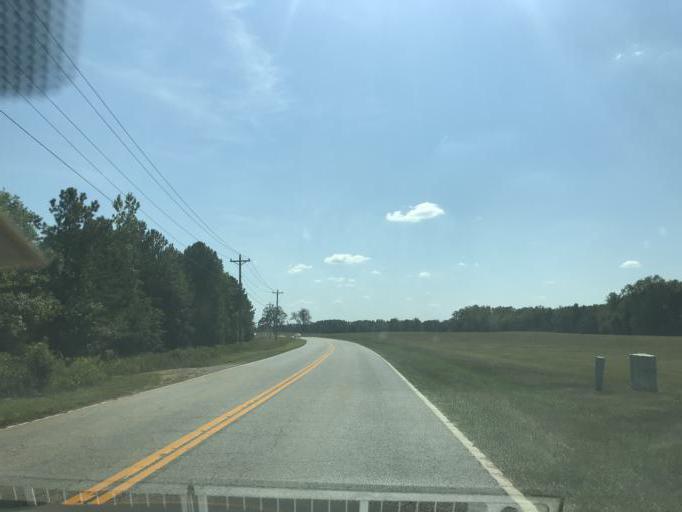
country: US
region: South Carolina
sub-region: Cherokee County
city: Gaffney
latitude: 35.0950
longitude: -81.7104
